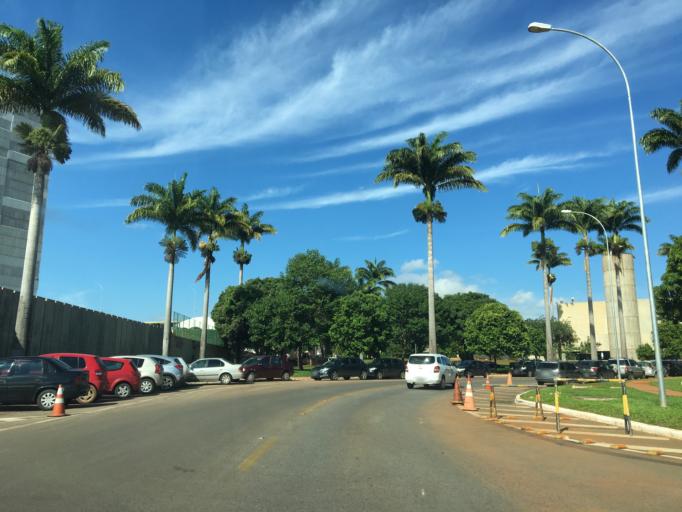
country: BR
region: Federal District
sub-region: Brasilia
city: Brasilia
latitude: -15.7982
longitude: -47.8619
